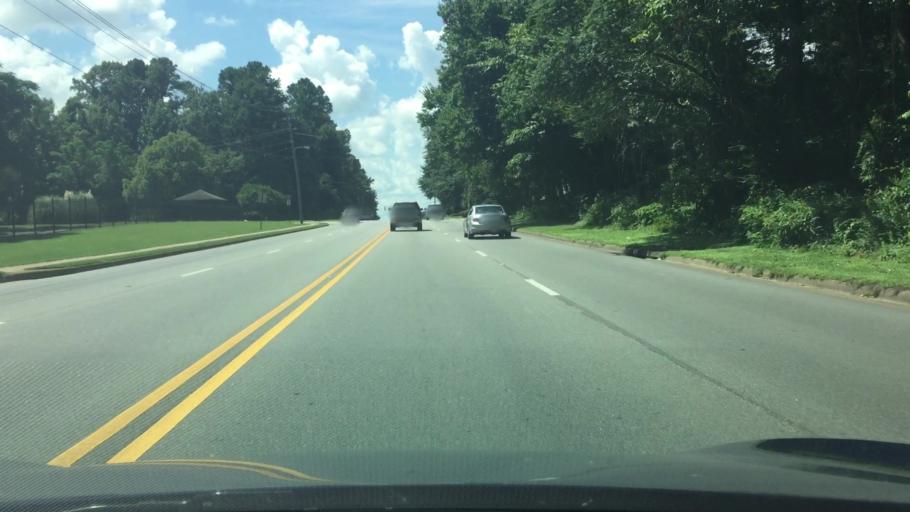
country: US
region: Alabama
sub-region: Lee County
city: Auburn
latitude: 32.6202
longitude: -85.4476
